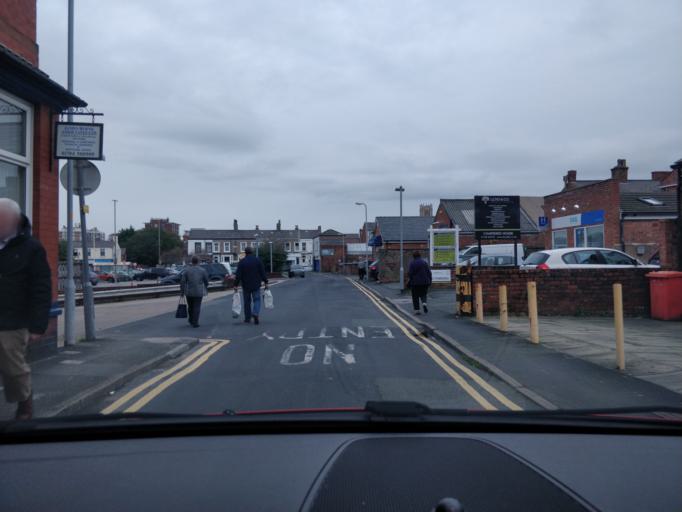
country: GB
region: England
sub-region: Sefton
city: Southport
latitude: 53.6487
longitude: -3.0023
